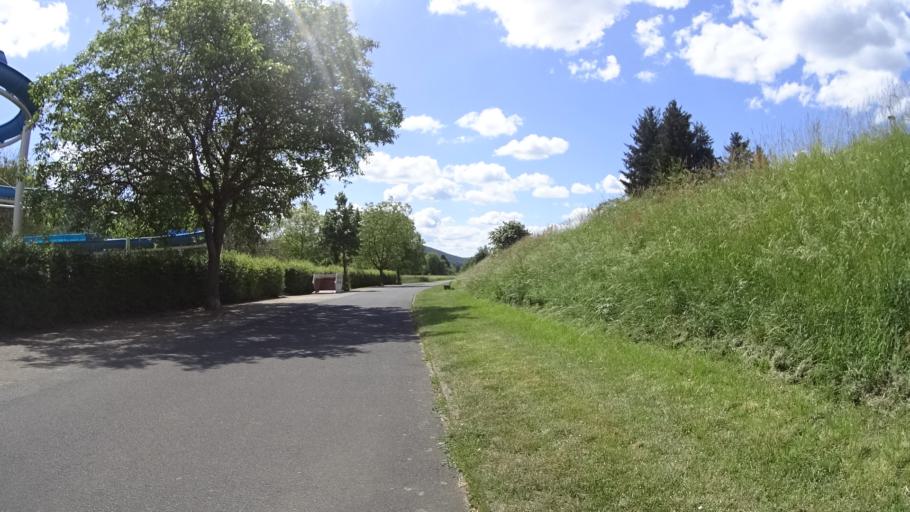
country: DE
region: Bavaria
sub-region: Regierungsbezirk Unterfranken
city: Klingenberg am Main
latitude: 49.7779
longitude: 9.1788
